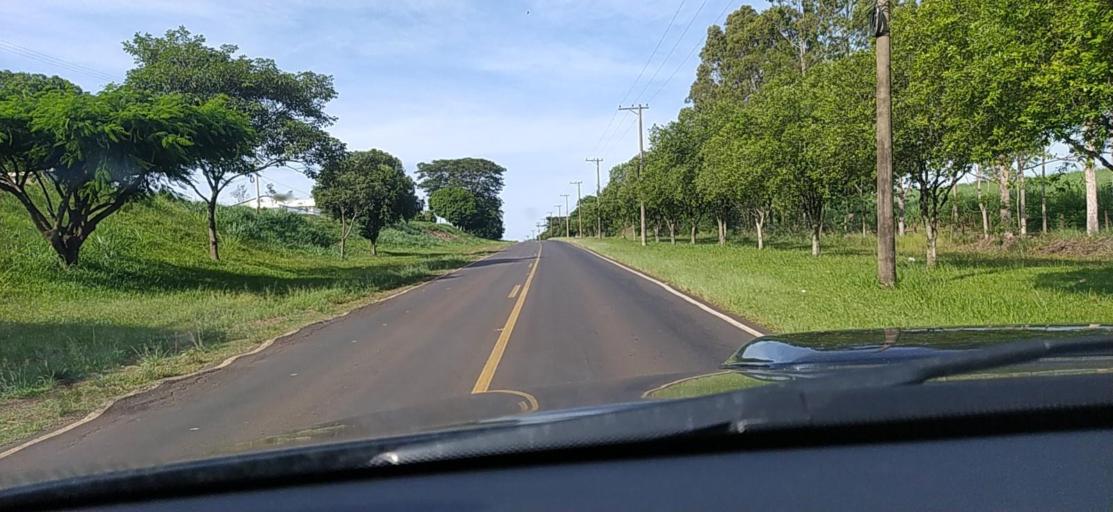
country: BR
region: Sao Paulo
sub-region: Pindorama
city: Pindorama
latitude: -21.1982
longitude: -48.9216
